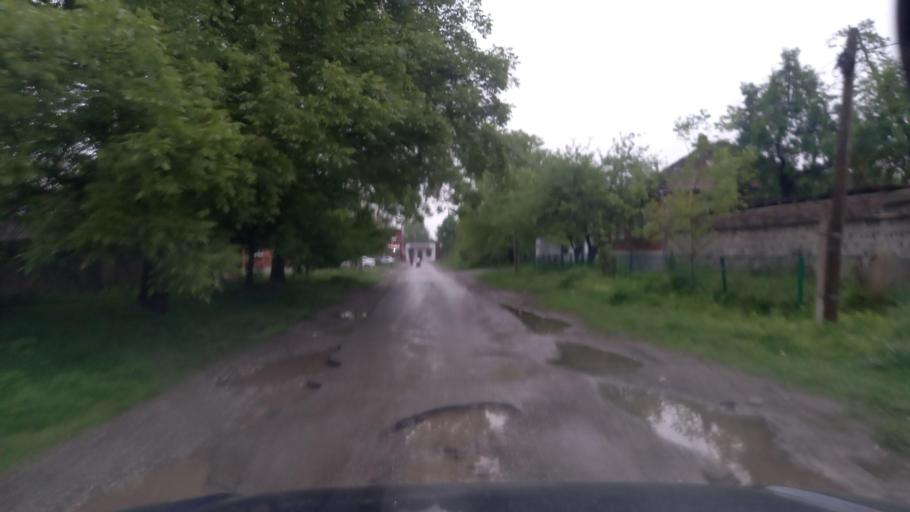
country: RU
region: North Ossetia
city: Alagir
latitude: 43.0458
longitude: 44.2228
